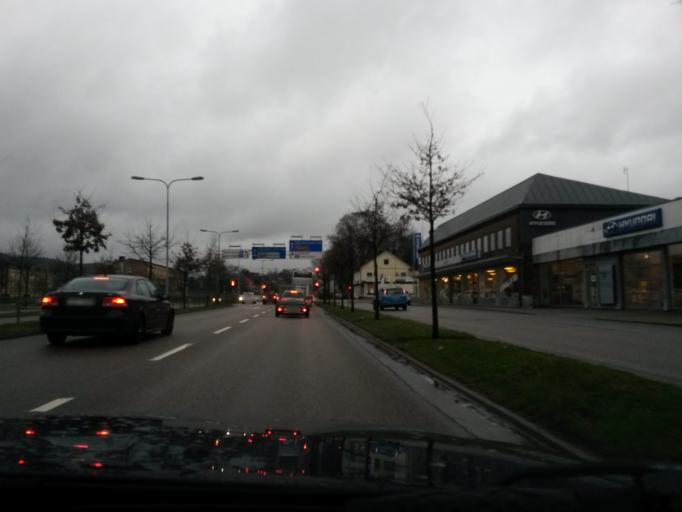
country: SE
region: Vaestra Goetaland
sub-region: Boras Kommun
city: Boras
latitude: 57.7358
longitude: 12.9372
